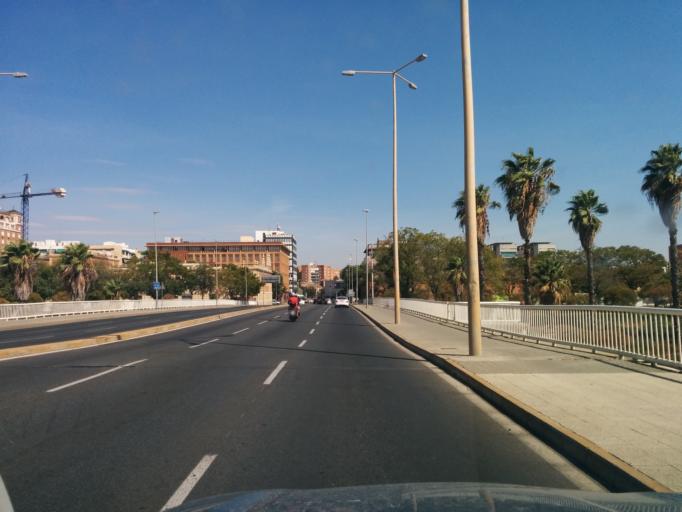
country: ES
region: Andalusia
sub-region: Provincia de Sevilla
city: Sevilla
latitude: 37.3676
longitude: -5.9918
